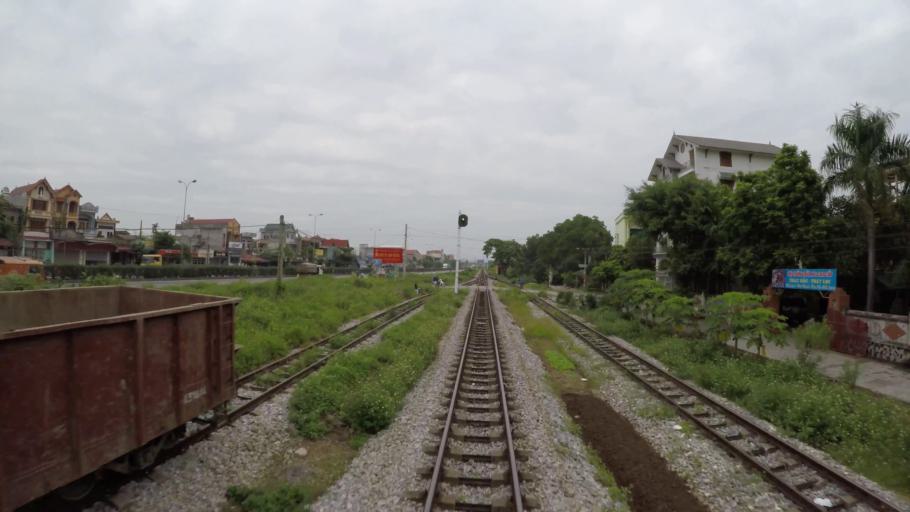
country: VN
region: Hai Duong
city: Nam Sach
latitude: 20.9728
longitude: 106.3861
